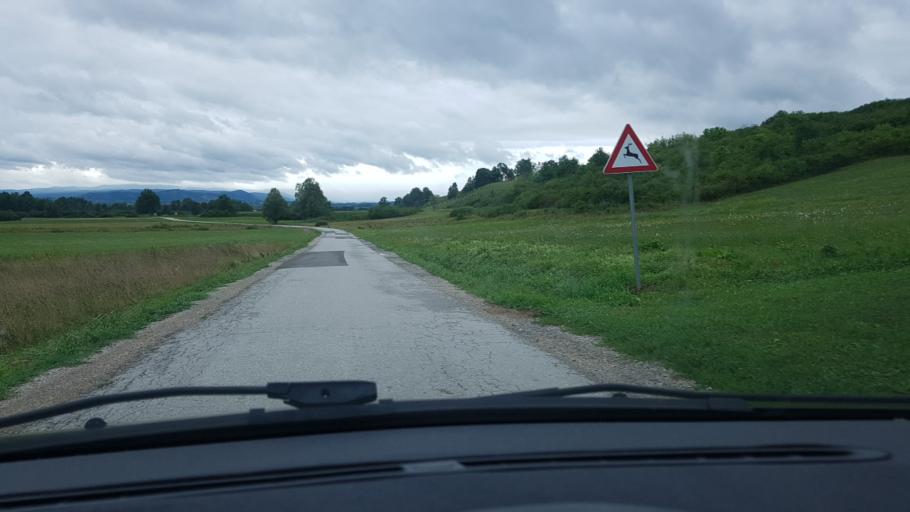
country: HR
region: Karlovacka
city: Ozalj
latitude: 45.5795
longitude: 15.5425
